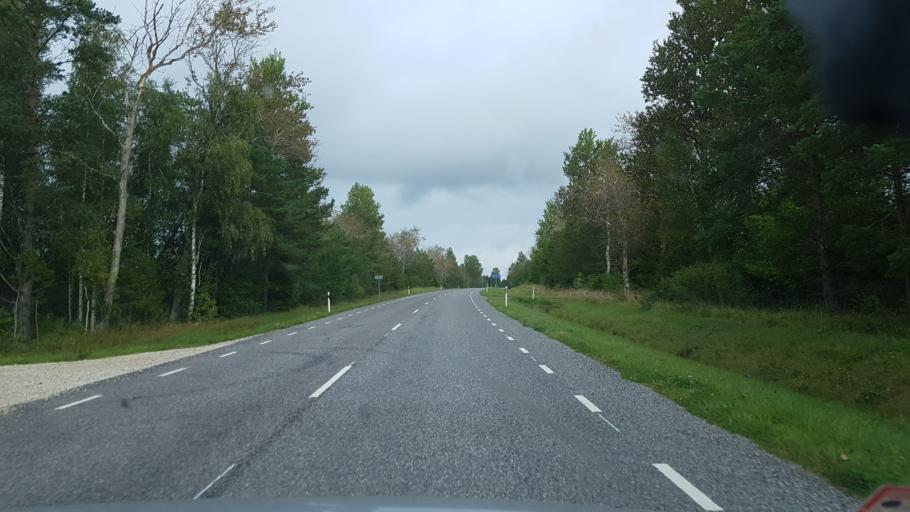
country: EE
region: Hiiumaa
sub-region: Kaerdla linn
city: Kardla
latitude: 58.9869
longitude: 22.5143
